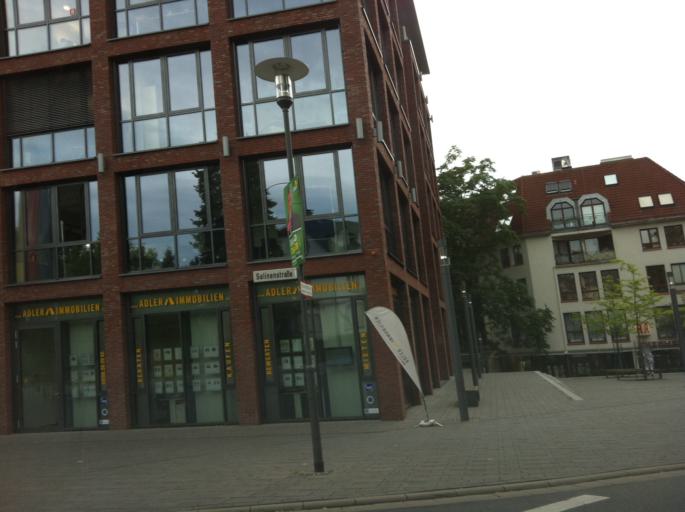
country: DE
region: Hesse
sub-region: Regierungsbezirk Darmstadt
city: Bad Soden am Taunus
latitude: 50.1441
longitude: 8.5040
